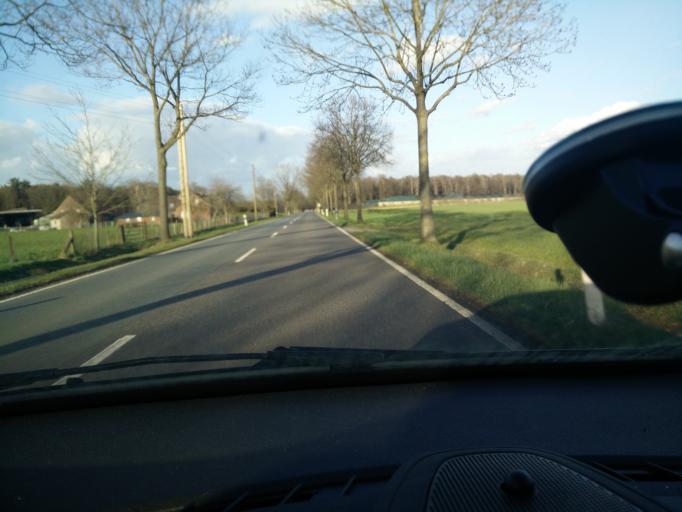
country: DE
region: North Rhine-Westphalia
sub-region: Regierungsbezirk Munster
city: Rhede
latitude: 51.7459
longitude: 6.7392
